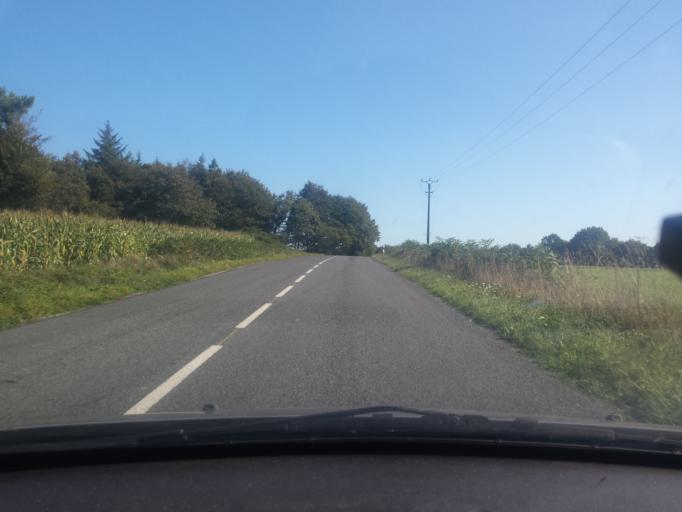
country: FR
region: Brittany
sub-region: Departement des Cotes-d'Armor
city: Gouarec
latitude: 48.1768
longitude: -3.1675
